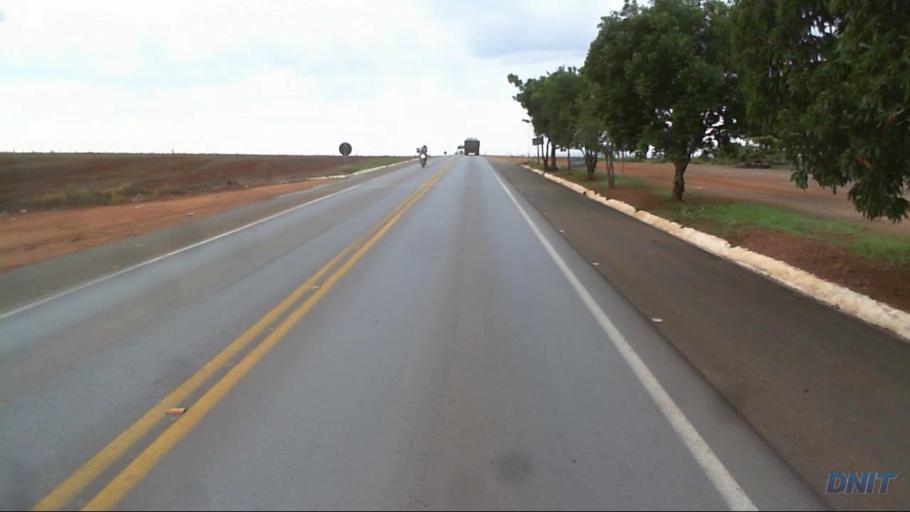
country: BR
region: Goias
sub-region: Uruacu
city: Uruacu
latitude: -14.6379
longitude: -49.1746
